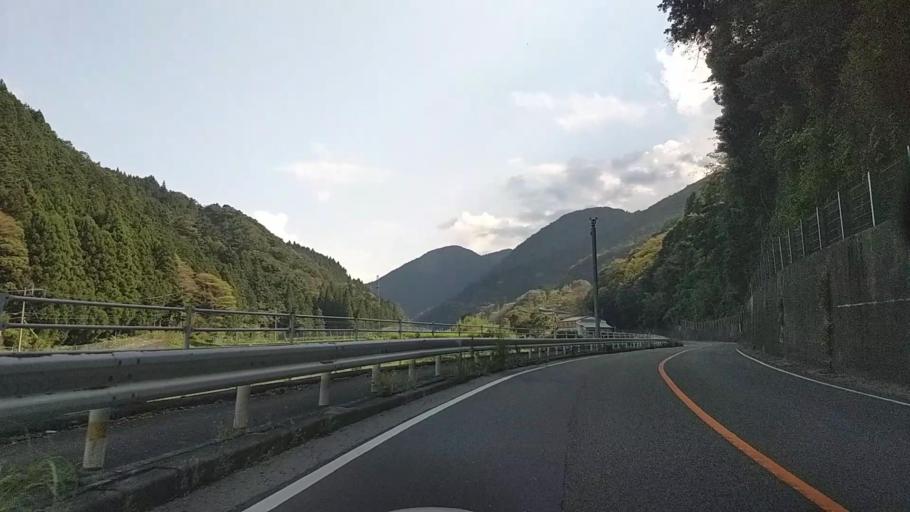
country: JP
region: Shizuoka
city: Fujinomiya
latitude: 35.3442
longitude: 138.4241
